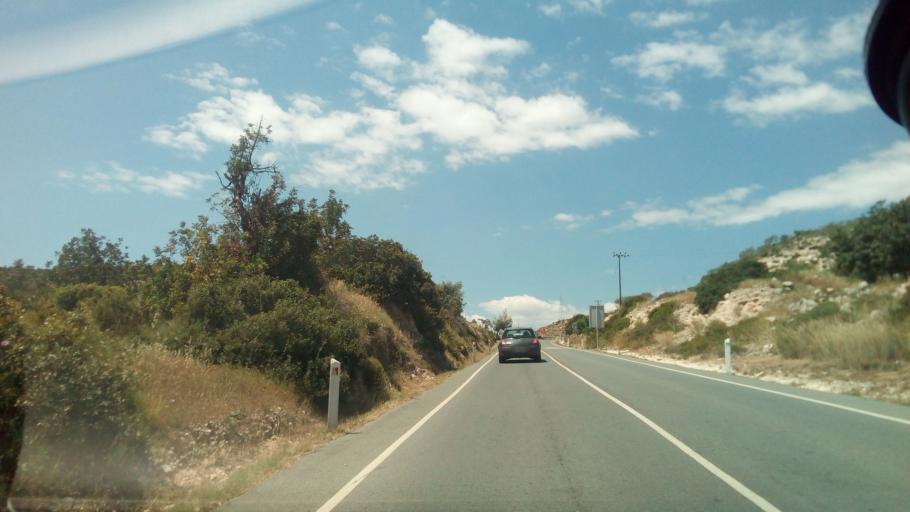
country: CY
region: Limassol
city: Erimi
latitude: 34.6956
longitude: 32.9033
